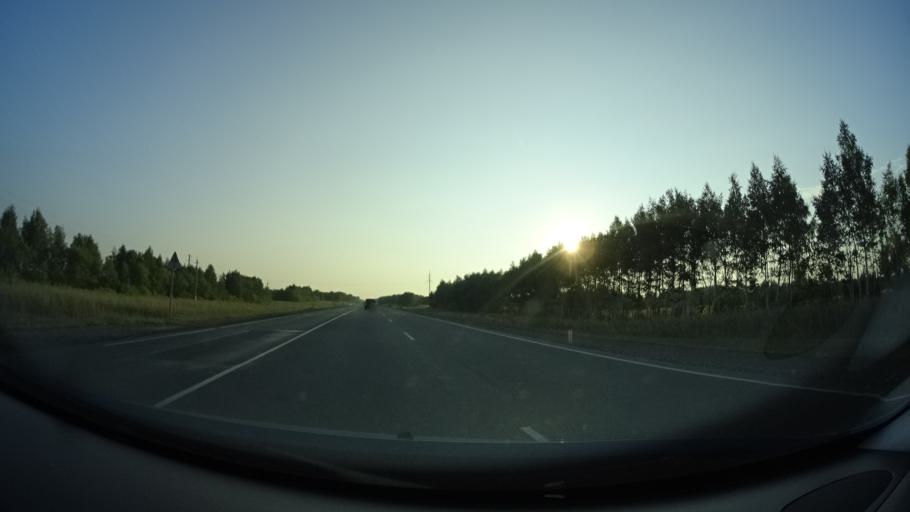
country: RU
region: Samara
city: Isakly
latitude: 54.0166
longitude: 51.7638
